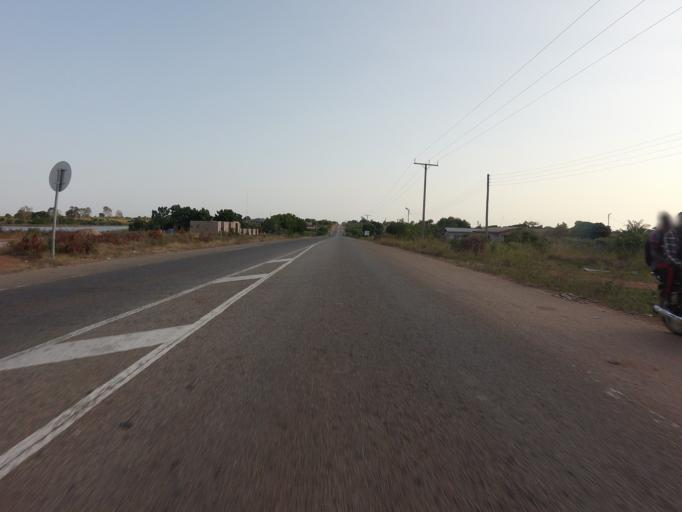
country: GH
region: Volta
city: Anloga
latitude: 6.0234
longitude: 0.6011
